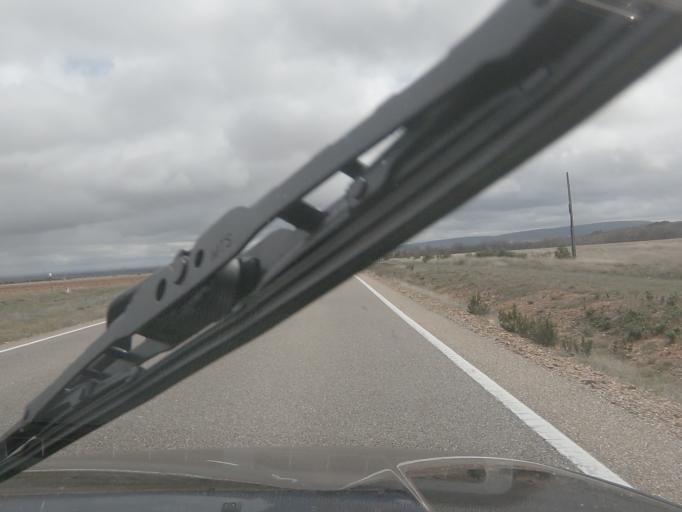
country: ES
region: Castille and Leon
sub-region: Provincia de Zamora
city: Tabara
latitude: 41.8464
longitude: -5.9811
